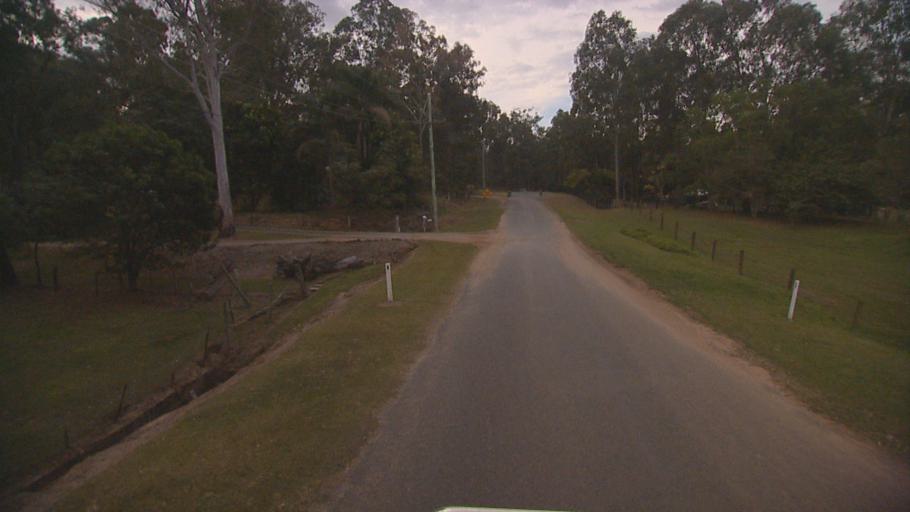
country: AU
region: Queensland
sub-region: Logan
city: Chambers Flat
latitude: -27.8193
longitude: 153.0917
